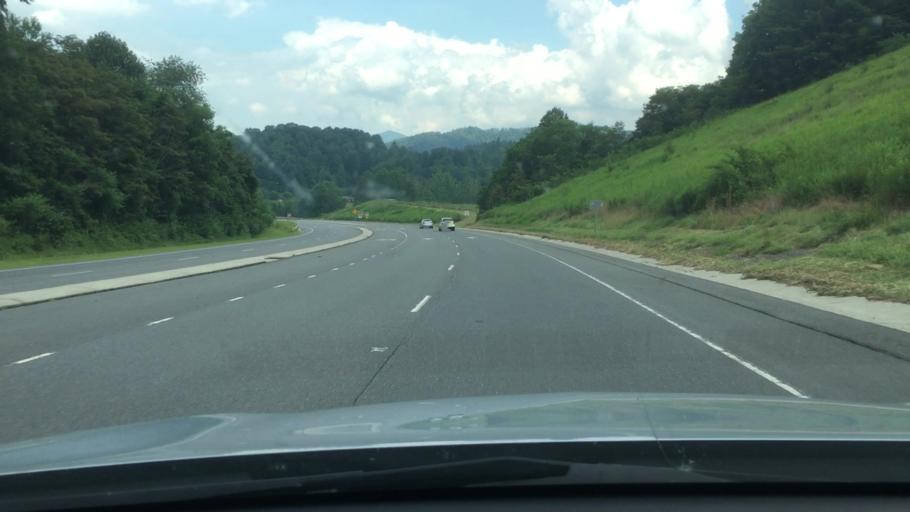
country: US
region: North Carolina
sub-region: Yancey County
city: Burnsville
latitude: 35.9111
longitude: -82.3888
